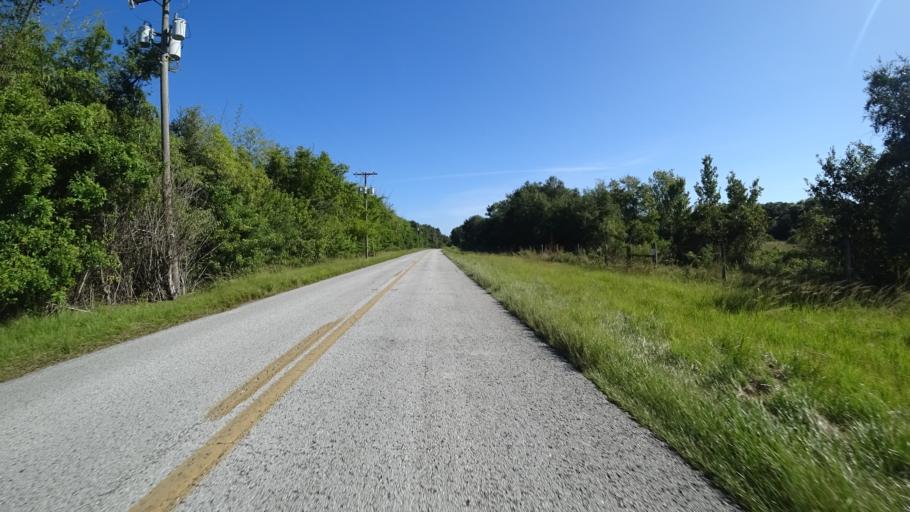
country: US
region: Florida
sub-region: Hillsborough County
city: Wimauma
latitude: 27.6597
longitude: -82.3126
